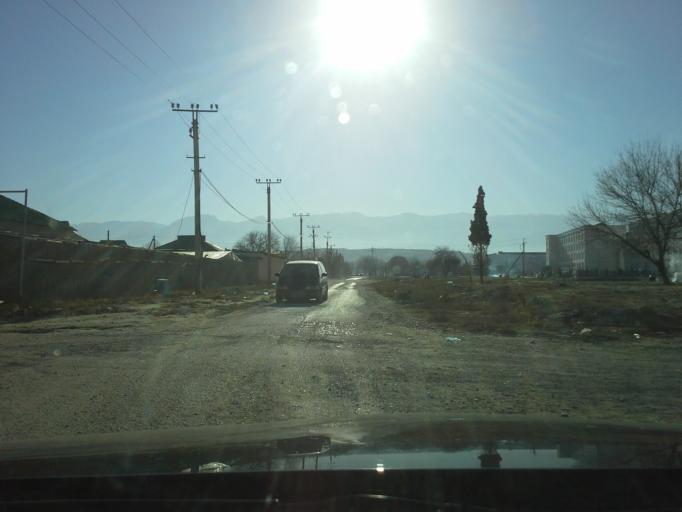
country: TM
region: Ahal
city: Ashgabat
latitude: 37.9691
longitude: 58.3384
